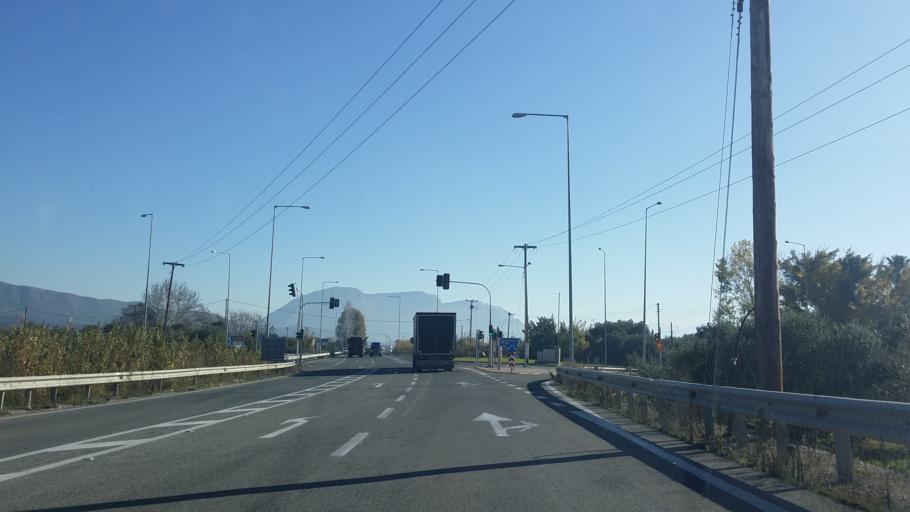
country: GR
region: West Greece
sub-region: Nomos Aitolias kai Akarnanias
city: Mesolongi
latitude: 38.3807
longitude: 21.4591
